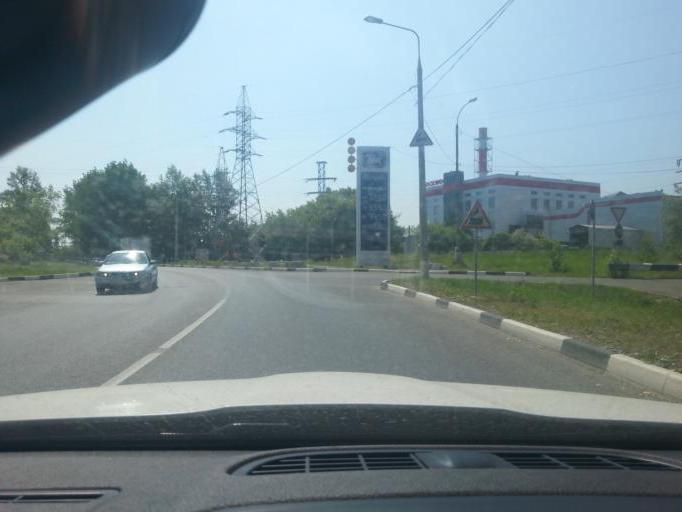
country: RU
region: Moskovskaya
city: Zheleznodorozhnyy
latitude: 55.7333
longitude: 38.0102
